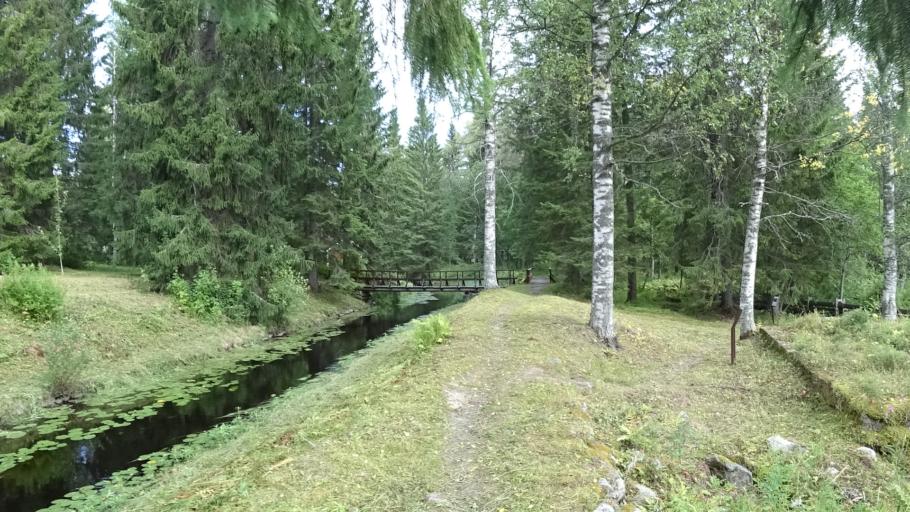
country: FI
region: North Karelia
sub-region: Joensuu
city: Ilomantsi
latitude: 62.6411
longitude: 31.2921
